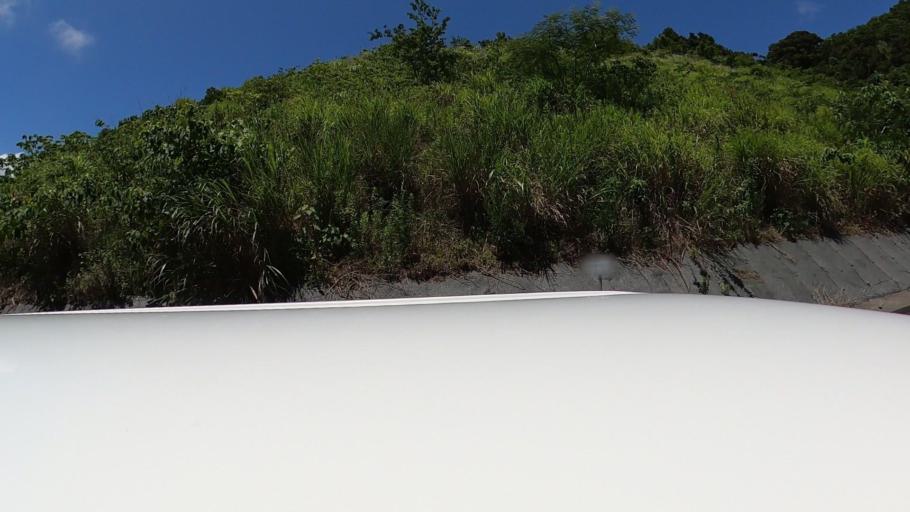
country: JP
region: Miyazaki
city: Takanabe
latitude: 32.3451
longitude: 131.6003
